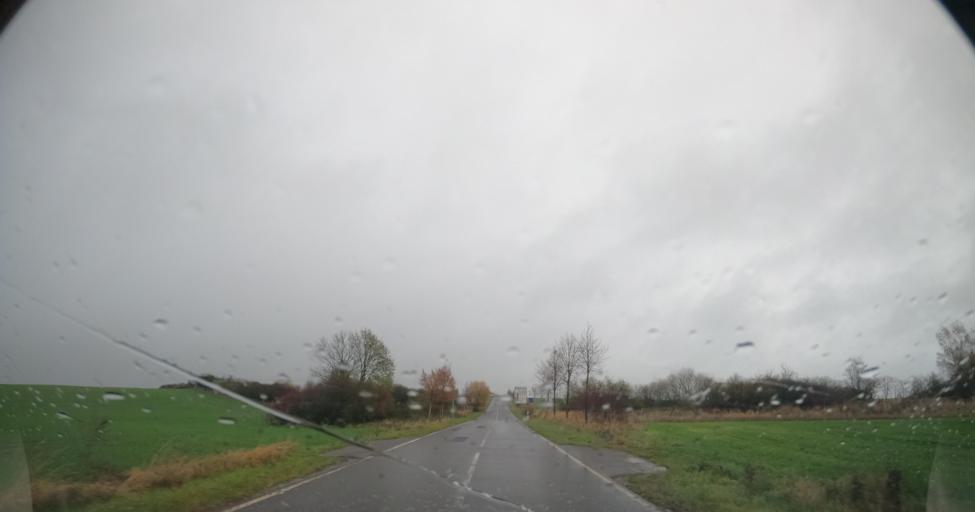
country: PL
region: West Pomeranian Voivodeship
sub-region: Powiat policki
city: Kolbaskowo
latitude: 53.3738
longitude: 14.3944
